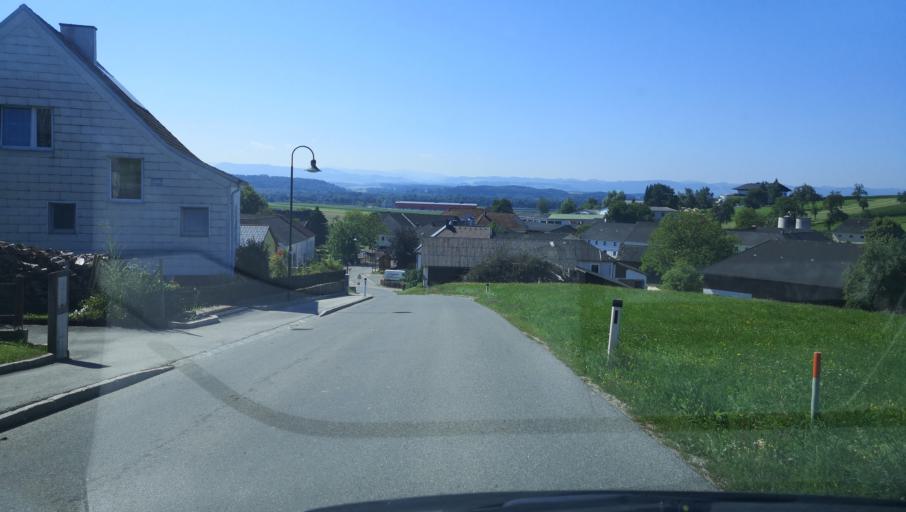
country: AT
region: Lower Austria
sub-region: Politischer Bezirk Melk
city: Neumarkt an der Ybbs
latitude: 48.1478
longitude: 15.0290
